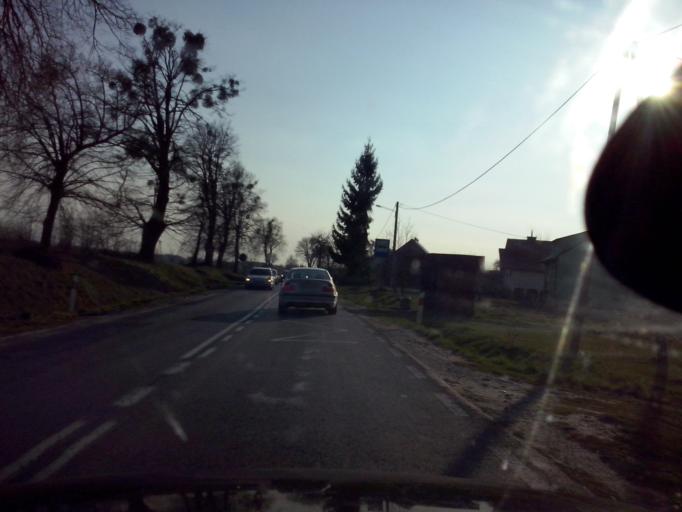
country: PL
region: Lublin Voivodeship
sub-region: Powiat janowski
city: Modliborzyce
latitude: 50.7556
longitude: 22.2807
